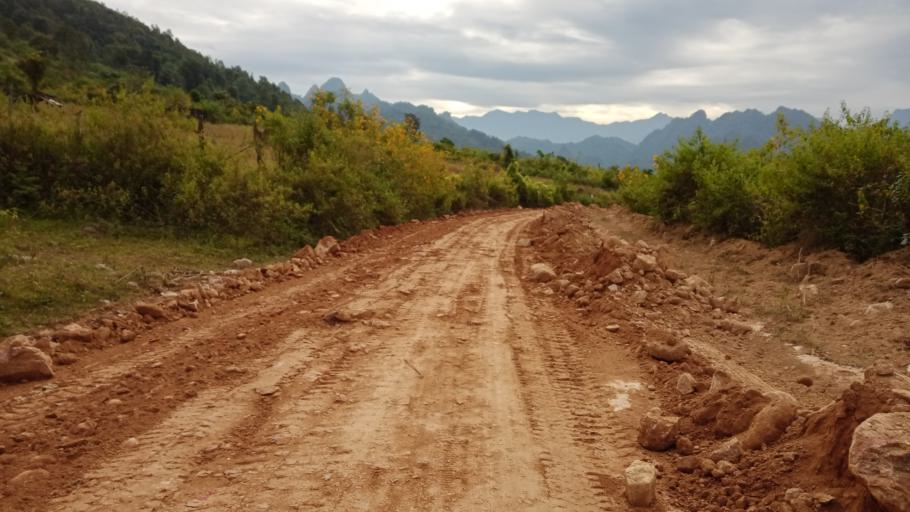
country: LA
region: Xiangkhoang
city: Phonsavan
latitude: 19.1164
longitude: 102.9236
